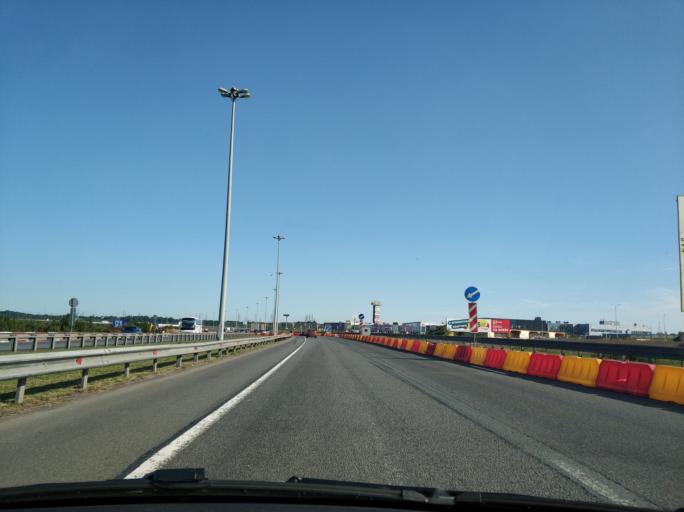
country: RU
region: Leningrad
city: Bugry
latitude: 60.0826
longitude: 30.3790
